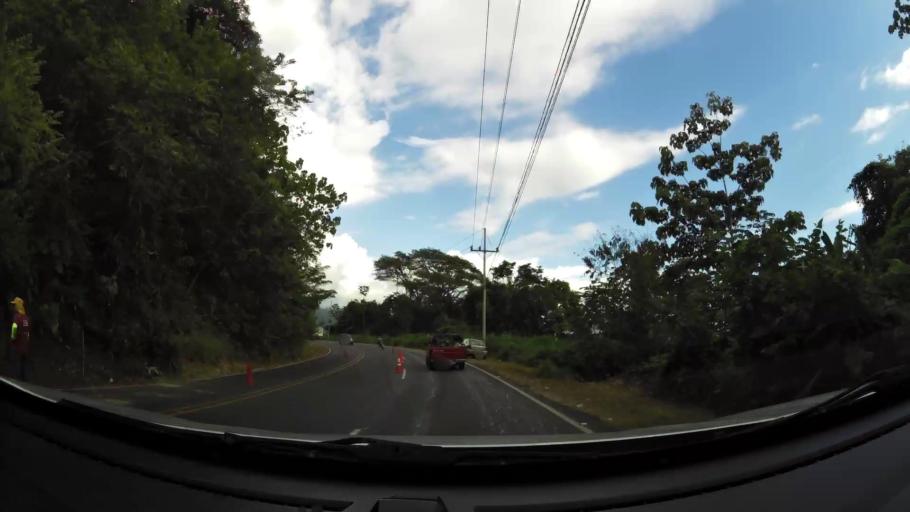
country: CR
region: Puntarenas
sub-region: Canton de Garabito
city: Jaco
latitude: 9.6878
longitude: -84.6477
